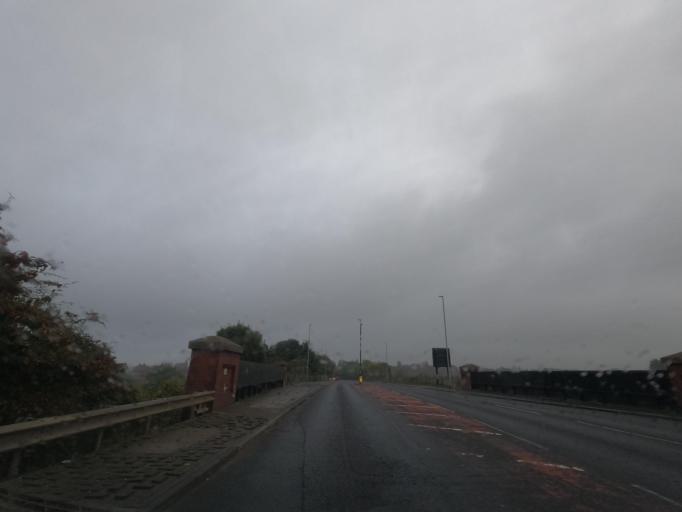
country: GB
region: England
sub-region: Middlesbrough
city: Middlesbrough
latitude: 54.5663
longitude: -1.2155
